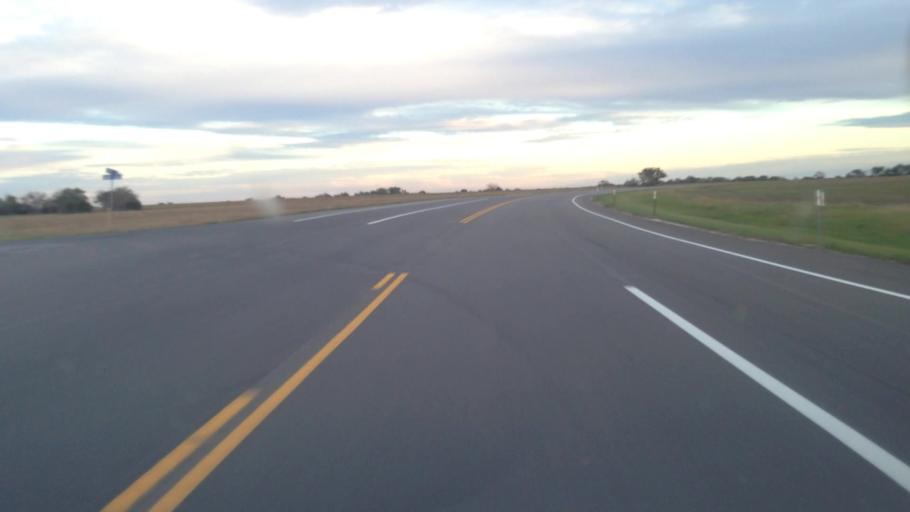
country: US
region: Kansas
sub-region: Franklin County
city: Ottawa
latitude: 38.4628
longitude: -95.2526
